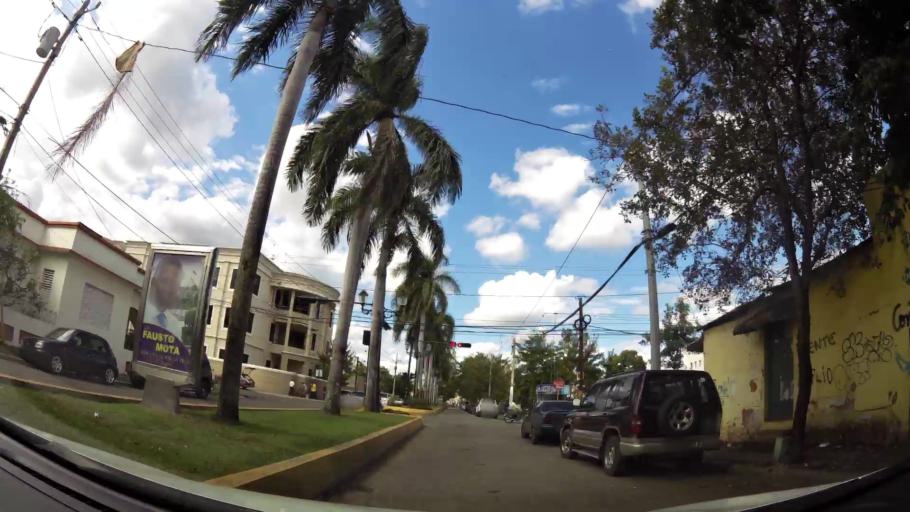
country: DO
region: La Vega
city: Concepcion de La Vega
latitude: 19.2222
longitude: -70.5306
